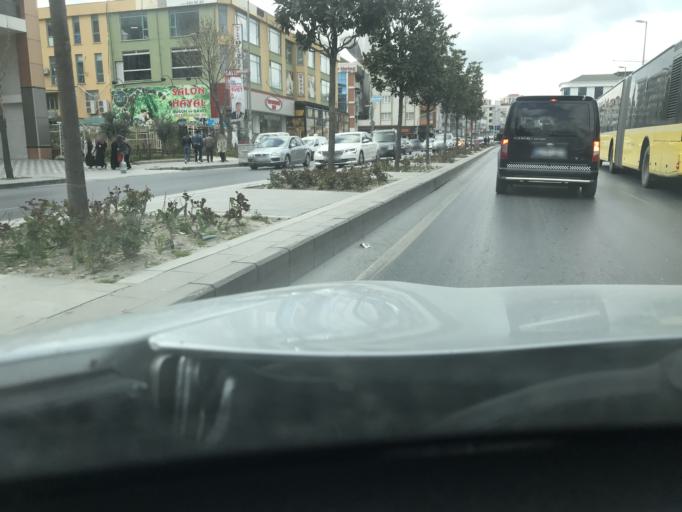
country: TR
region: Istanbul
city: Esenyurt
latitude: 41.0409
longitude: 28.6770
